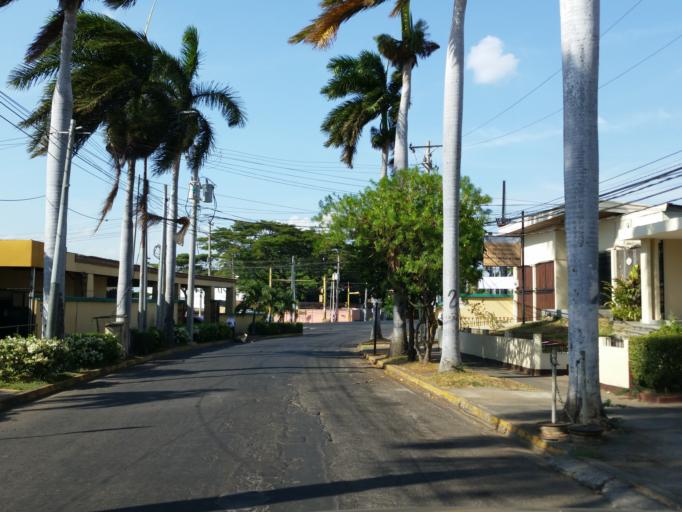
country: NI
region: Managua
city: Managua
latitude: 12.1189
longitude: -86.2613
